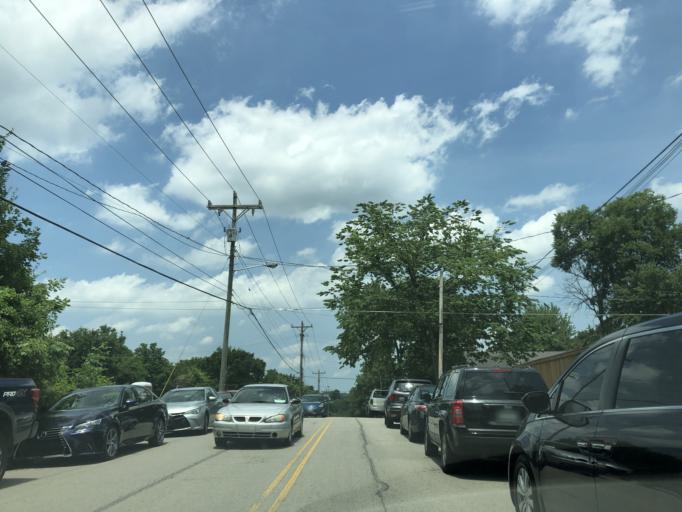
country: US
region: Tennessee
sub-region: Davidson County
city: Nashville
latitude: 36.1855
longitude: -86.7543
